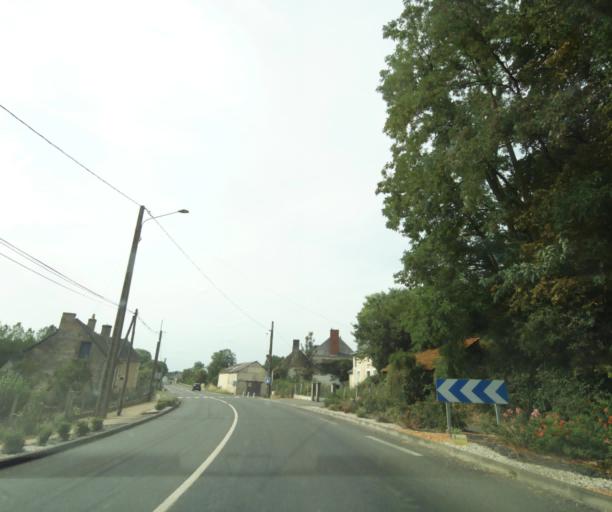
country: FR
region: Centre
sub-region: Departement d'Indre-et-Loire
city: Saint-Christophe-sur-le-Nais
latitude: 47.6625
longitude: 0.4758
